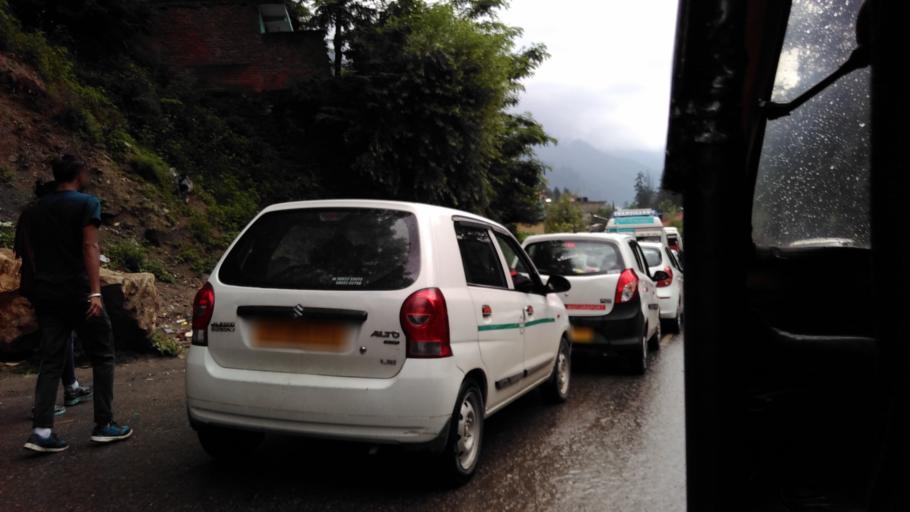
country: IN
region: Himachal Pradesh
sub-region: Kulu
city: Manali
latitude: 32.2515
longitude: 77.1898
